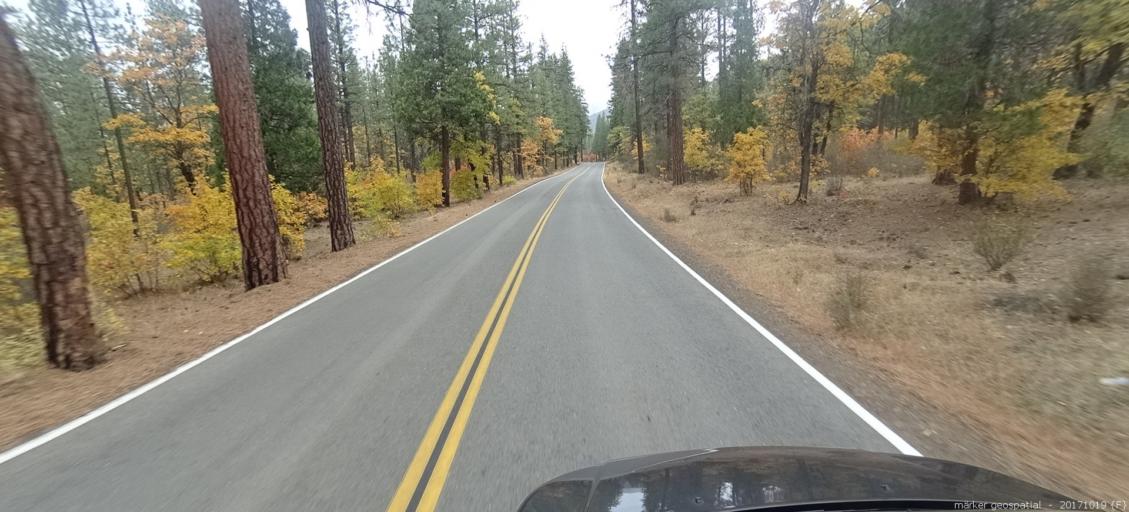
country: US
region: California
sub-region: Shasta County
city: Burney
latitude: 41.1814
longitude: -121.3629
